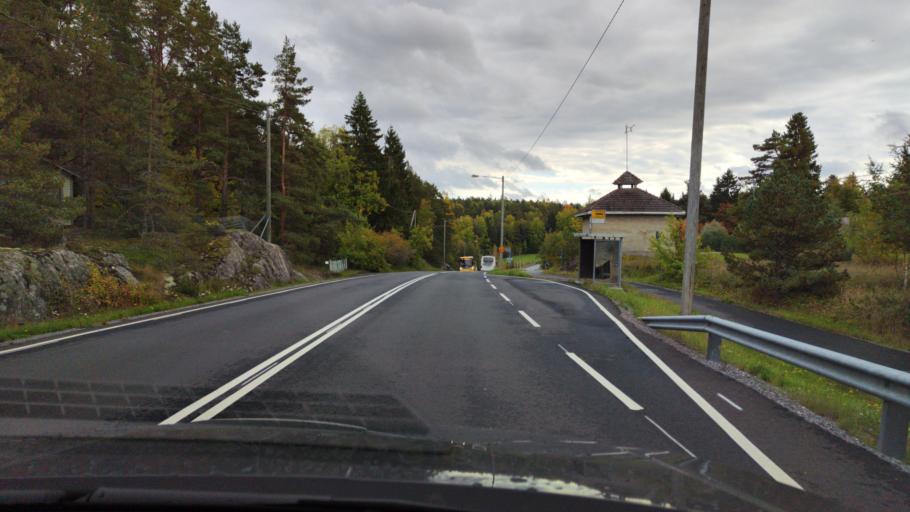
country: FI
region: Varsinais-Suomi
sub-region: Turku
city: Raisio
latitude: 60.3670
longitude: 22.1758
